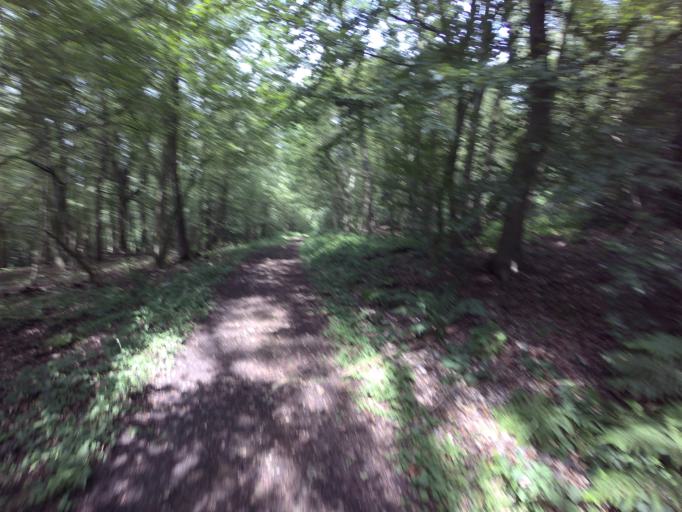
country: BE
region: Wallonia
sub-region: Province de Liege
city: Plombieres
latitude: 50.7550
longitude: 5.9803
